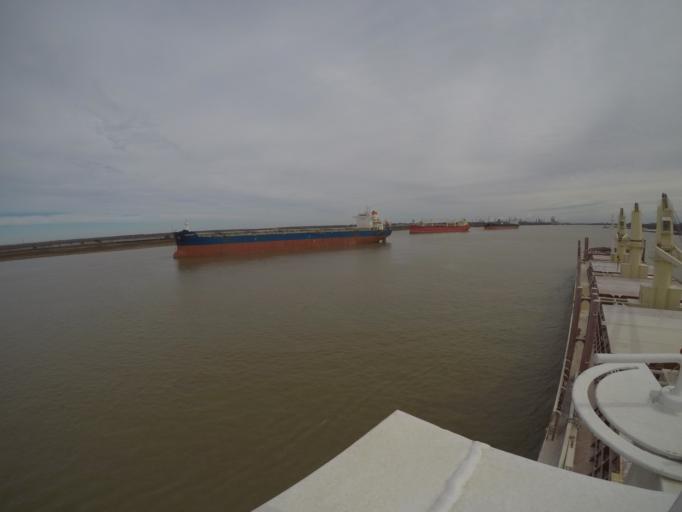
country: US
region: Louisiana
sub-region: Saint Charles Parish
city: Montz
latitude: 29.9948
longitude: -90.4436
